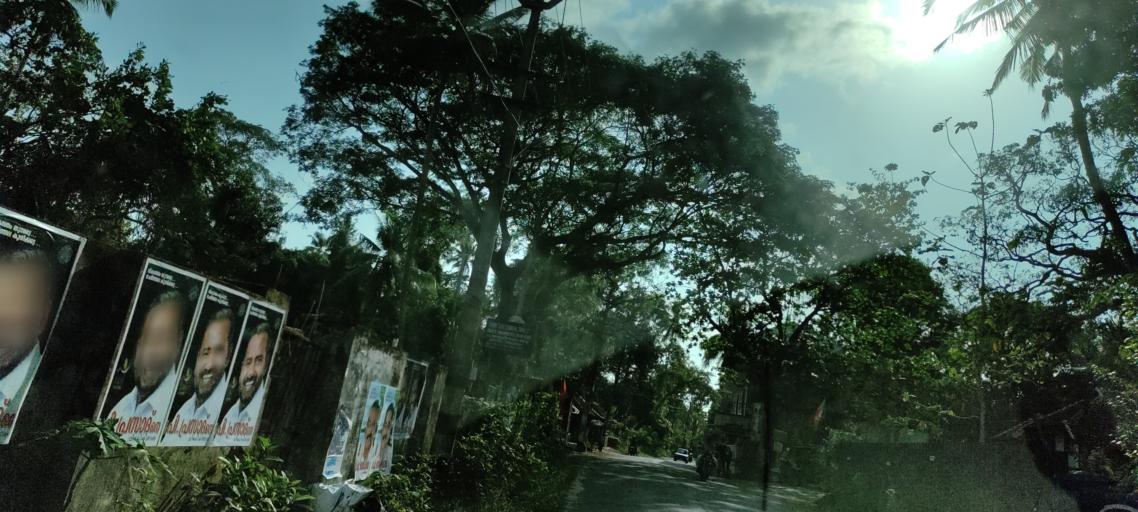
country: IN
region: Kerala
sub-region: Alappuzha
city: Vayalar
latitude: 9.6871
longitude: 76.3100
